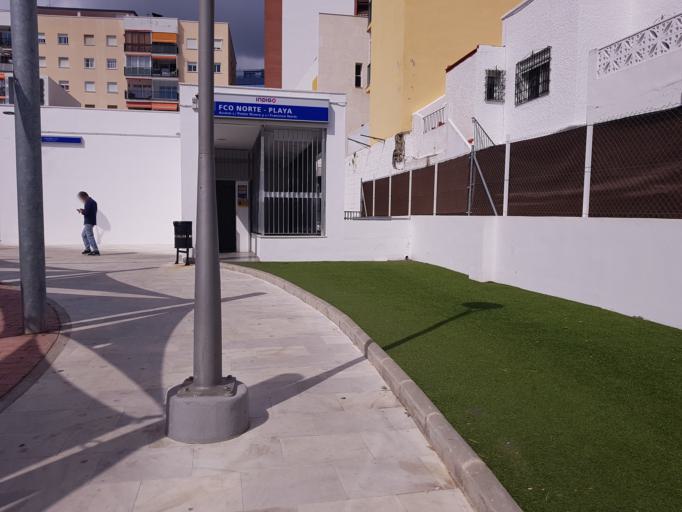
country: ES
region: Andalusia
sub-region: Provincia de Malaga
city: Marbella
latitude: 36.5088
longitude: -4.8892
